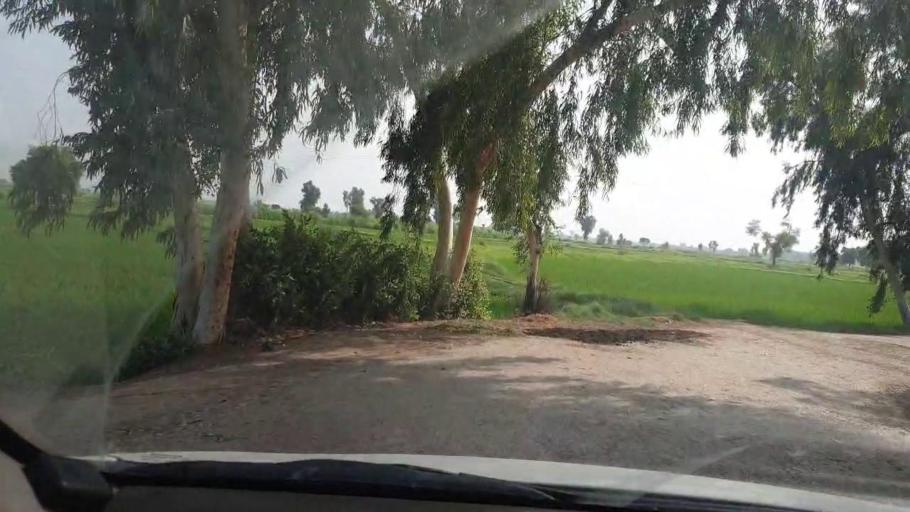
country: PK
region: Sindh
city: Lakhi
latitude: 27.8297
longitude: 68.7443
